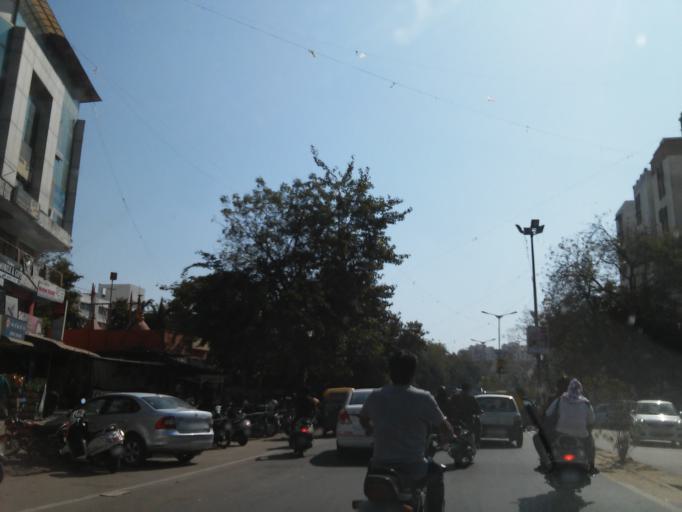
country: IN
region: Gujarat
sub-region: Ahmadabad
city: Sarkhej
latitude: 23.0368
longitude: 72.5279
